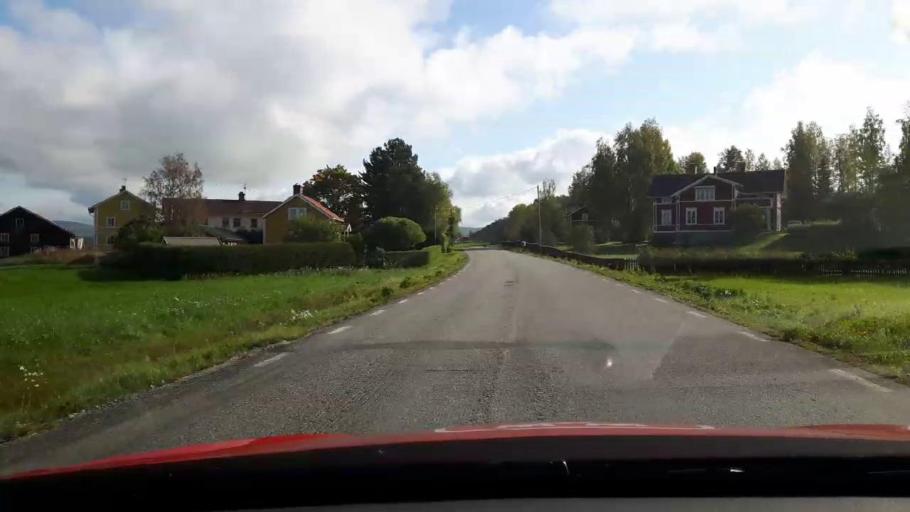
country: SE
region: Gaevleborg
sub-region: Ljusdals Kommun
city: Jaervsoe
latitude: 61.7527
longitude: 16.1387
